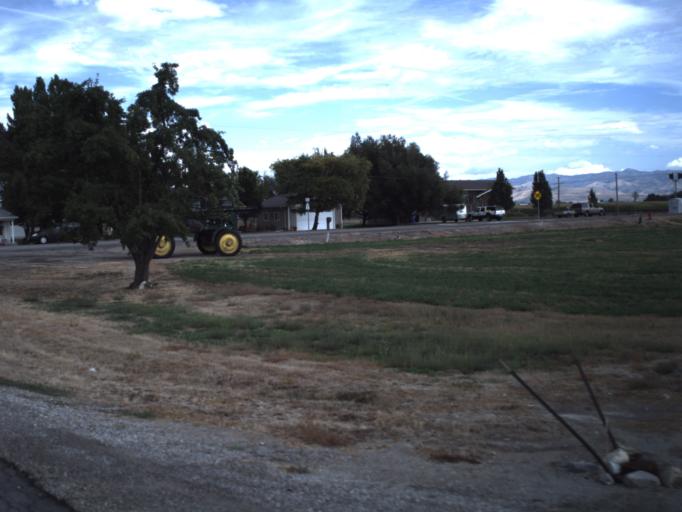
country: US
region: Utah
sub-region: Cache County
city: Lewiston
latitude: 41.9748
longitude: -111.9541
